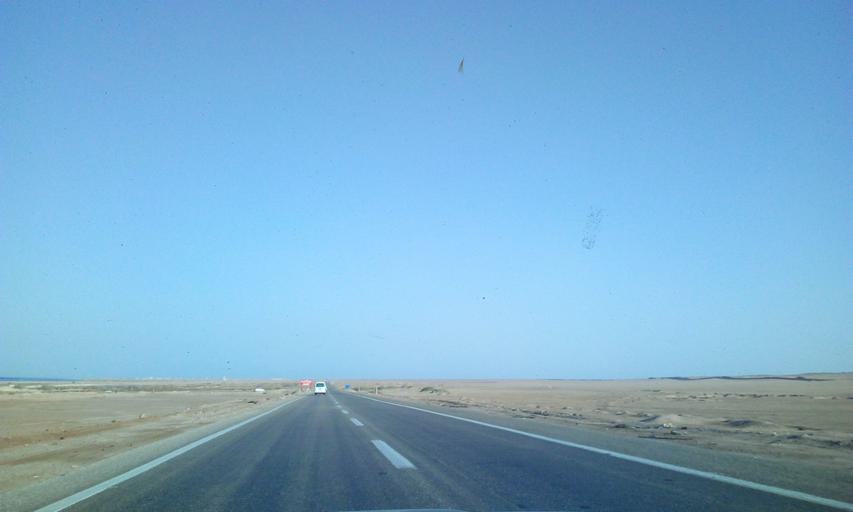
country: EG
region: South Sinai
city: Tor
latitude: 28.5689
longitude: 32.8659
